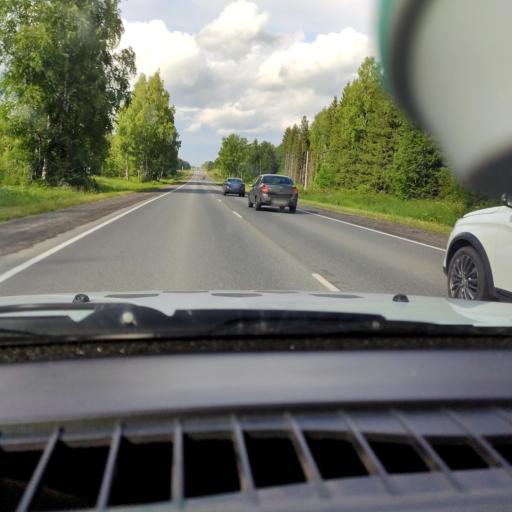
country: RU
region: Perm
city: Orda
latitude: 57.2523
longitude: 57.0010
